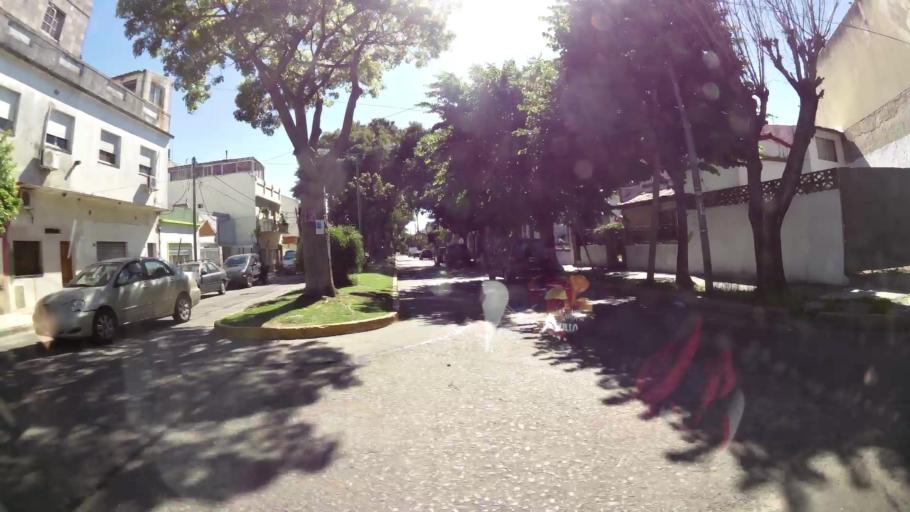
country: AR
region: Buenos Aires
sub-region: Partido de General San Martin
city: General San Martin
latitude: -34.5444
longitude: -58.5081
